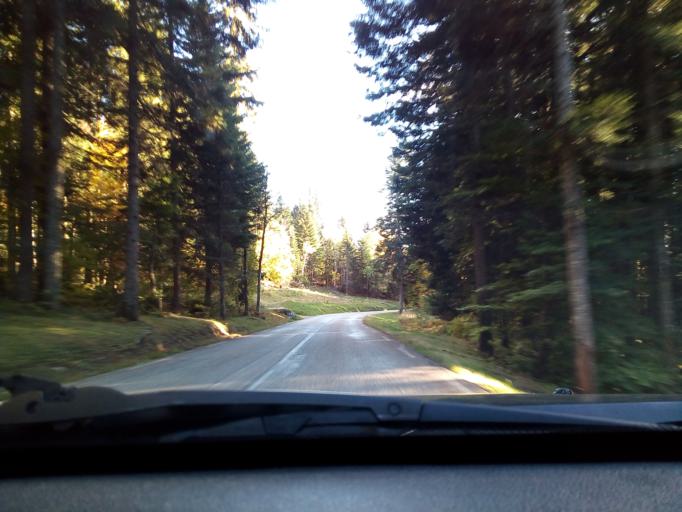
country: FR
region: Rhone-Alpes
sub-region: Departement de l'Isere
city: Le Sappey-en-Chartreuse
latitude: 45.2807
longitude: 5.7661
